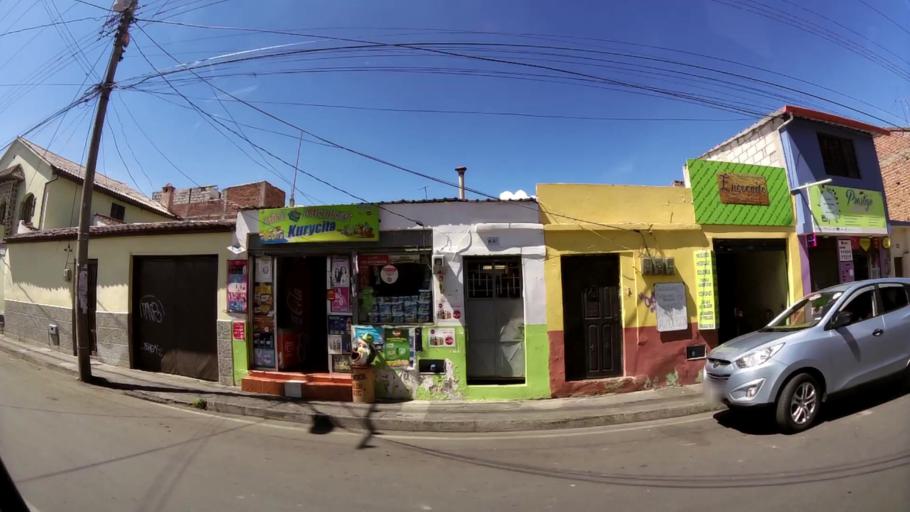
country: EC
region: Chimborazo
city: Riobamba
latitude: -1.6776
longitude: -78.6444
